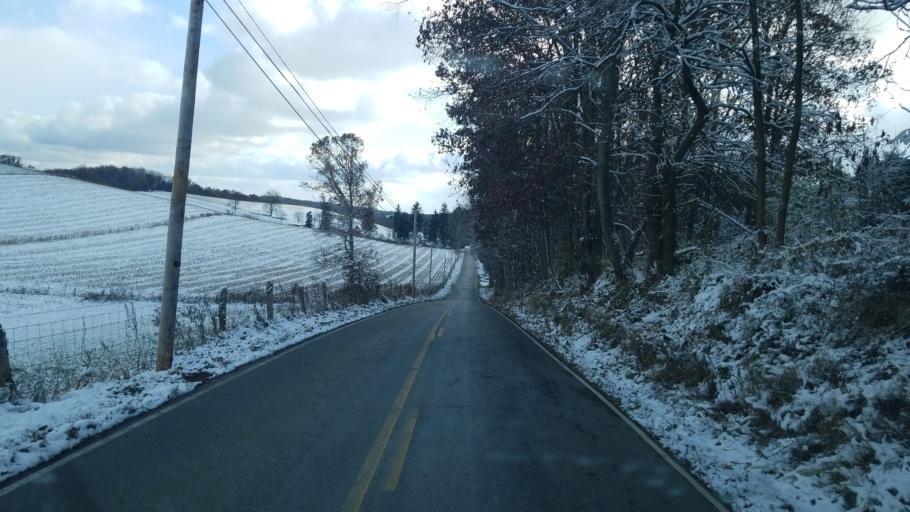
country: US
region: Ohio
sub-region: Licking County
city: Newark
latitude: 40.1578
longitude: -82.3767
